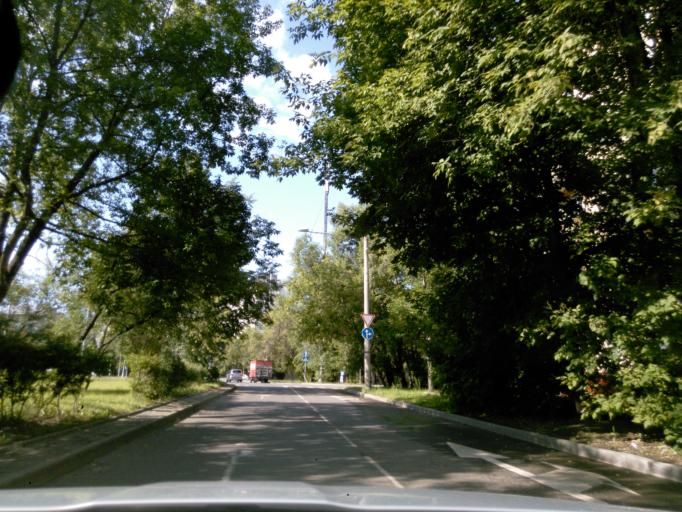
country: RU
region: Moskovskaya
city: Koptevo
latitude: 55.8321
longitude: 37.5268
